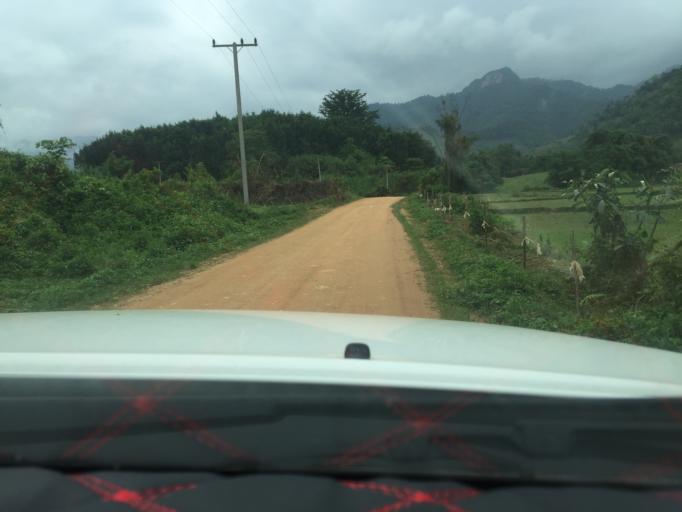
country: TH
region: Phayao
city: Phu Sang
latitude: 19.7358
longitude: 100.4765
